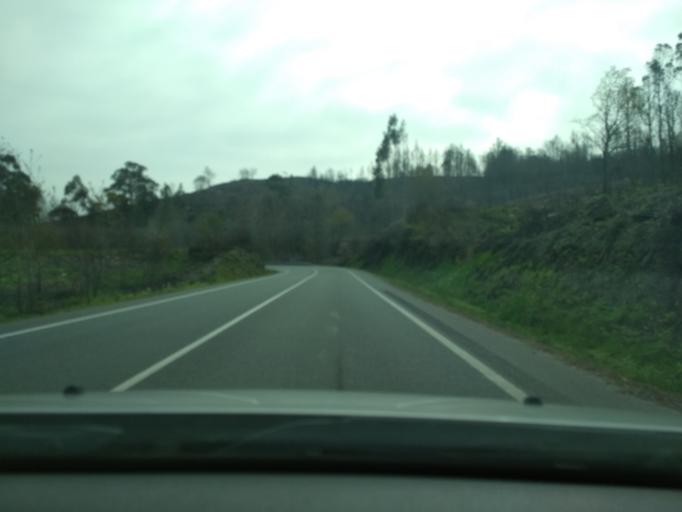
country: ES
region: Galicia
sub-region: Provincia de Pontevedra
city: Catoira
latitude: 42.6517
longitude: -8.6878
